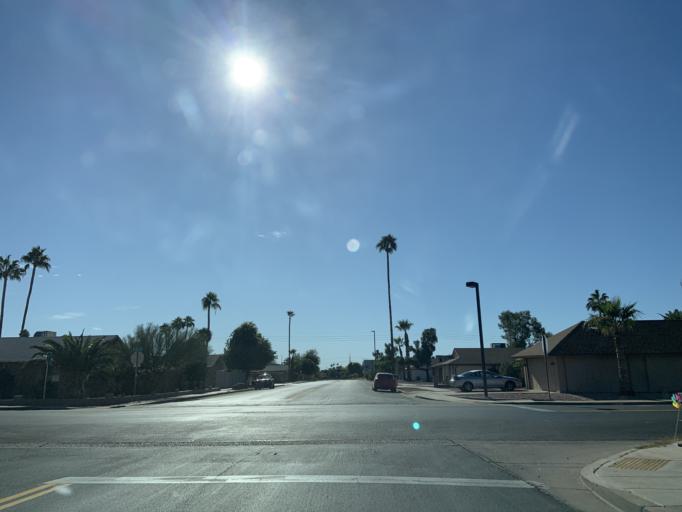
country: US
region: Arizona
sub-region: Maricopa County
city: San Carlos
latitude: 33.3663
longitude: -111.8679
